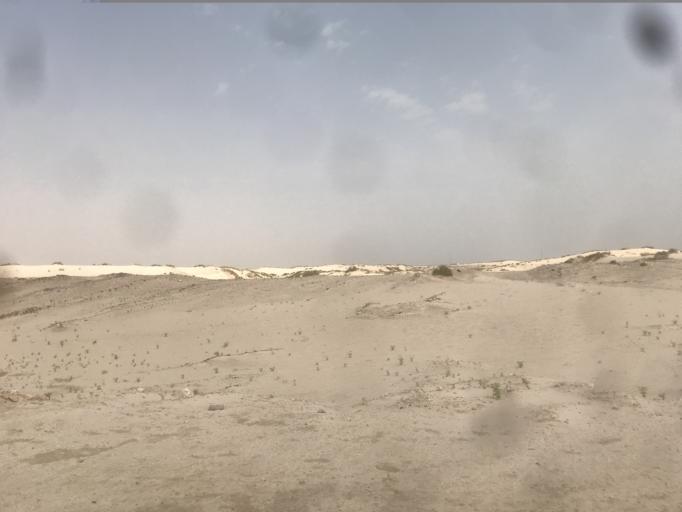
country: SA
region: Eastern Province
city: Abqaiq
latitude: 25.9068
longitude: 50.0012
